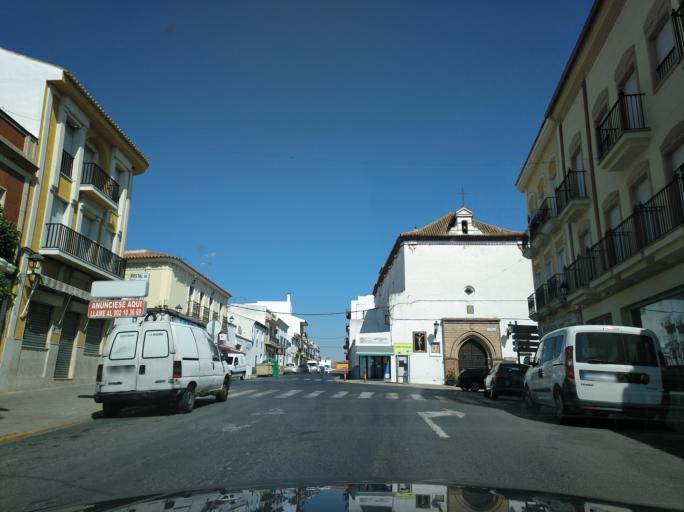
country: ES
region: Andalusia
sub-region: Provincia de Huelva
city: Gibraleon
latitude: 37.3758
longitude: -6.9675
